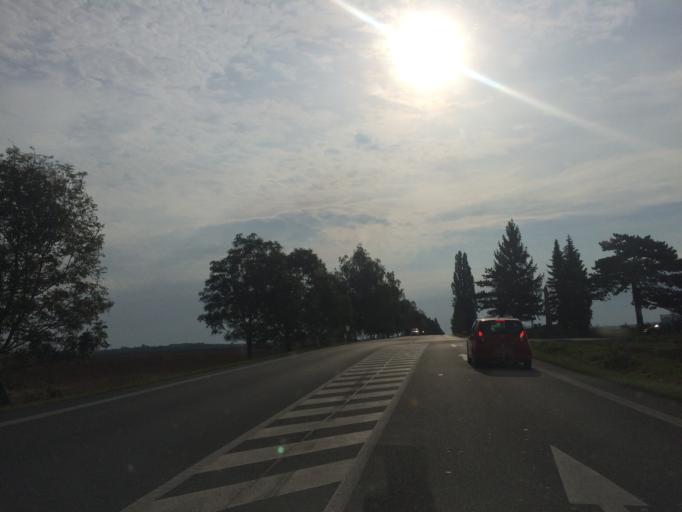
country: CZ
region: Central Bohemia
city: Cesky Brod
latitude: 50.0596
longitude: 14.8893
